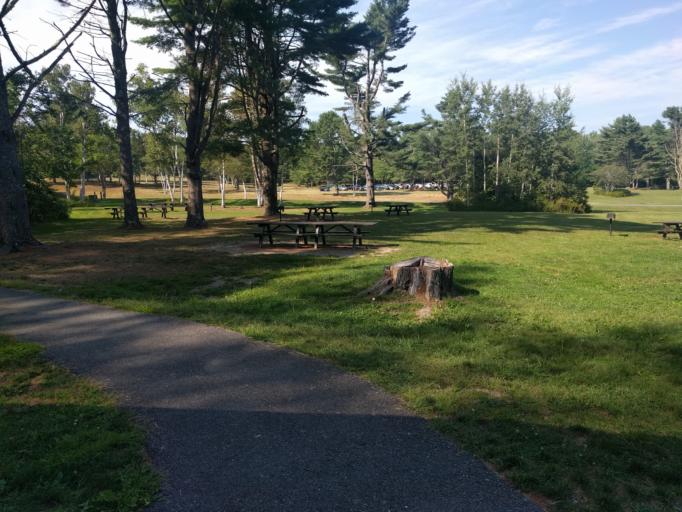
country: US
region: Maine
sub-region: Waldo County
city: Belfast
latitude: 44.4320
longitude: -68.9435
